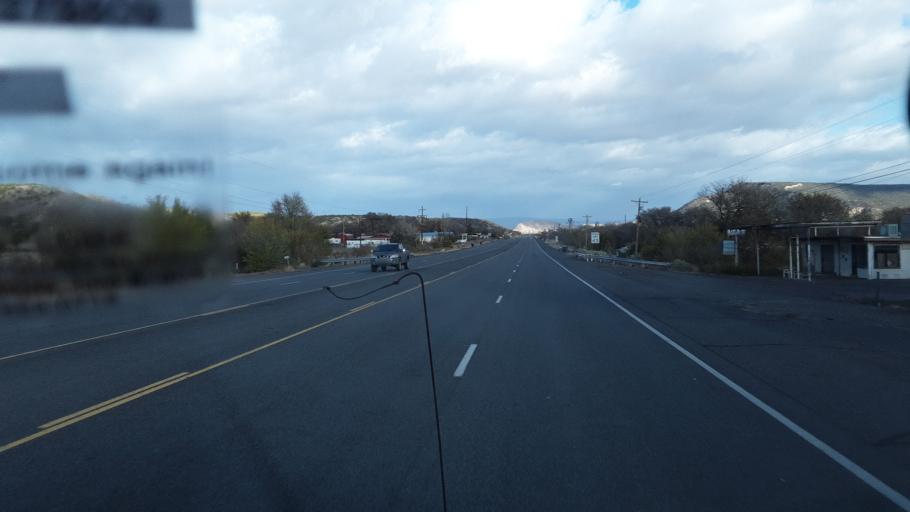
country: US
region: New Mexico
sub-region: Rio Arriba County
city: Ohkay Owingeh
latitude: 36.0559
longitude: -106.1163
